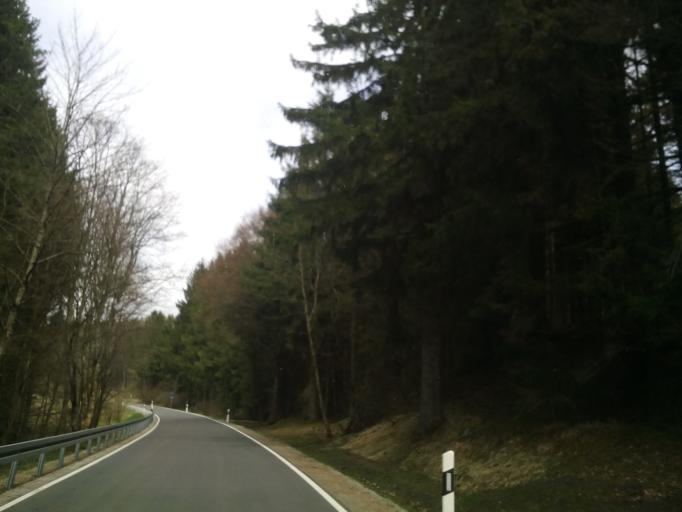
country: DE
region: Bavaria
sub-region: Regierungsbezirk Unterfranken
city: Bischofsheim an der Rhon
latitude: 50.4247
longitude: 10.0205
